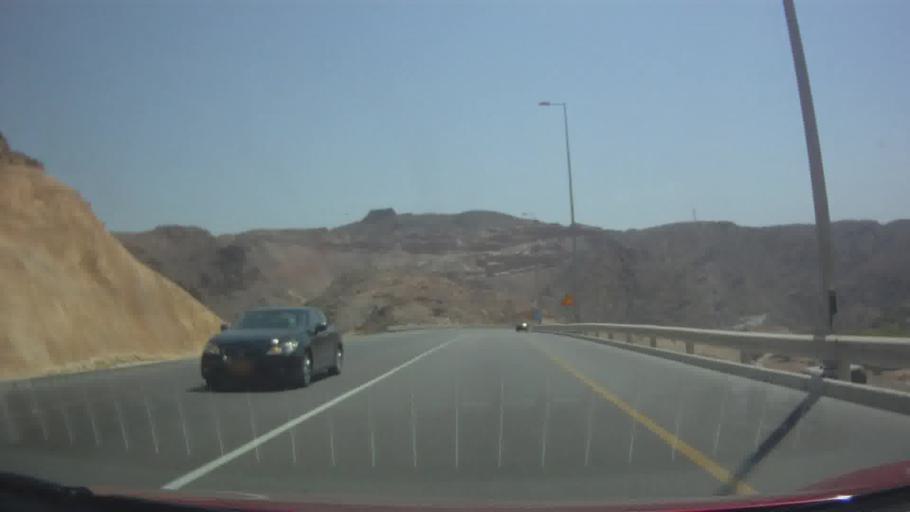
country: OM
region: Muhafazat Masqat
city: Muscat
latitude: 23.5380
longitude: 58.6488
